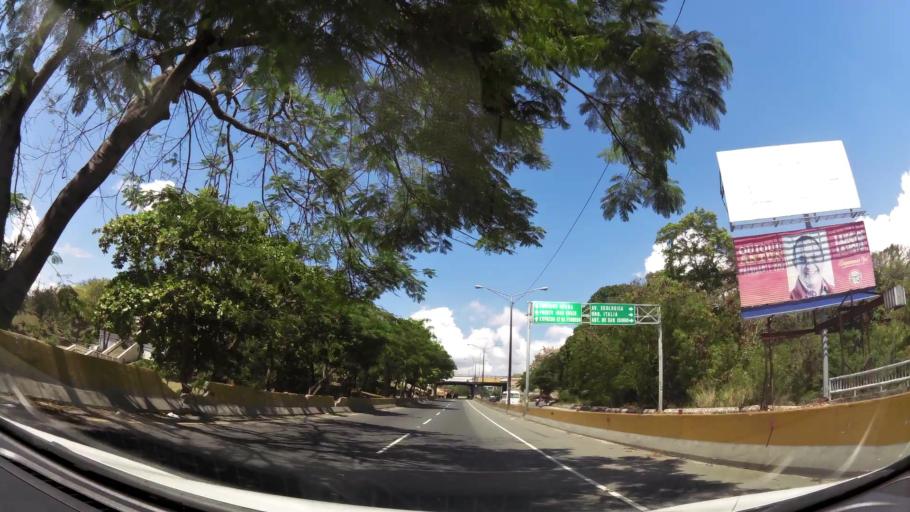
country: DO
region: Santo Domingo
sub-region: Santo Domingo
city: Santo Domingo Este
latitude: 18.4834
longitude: -69.8481
